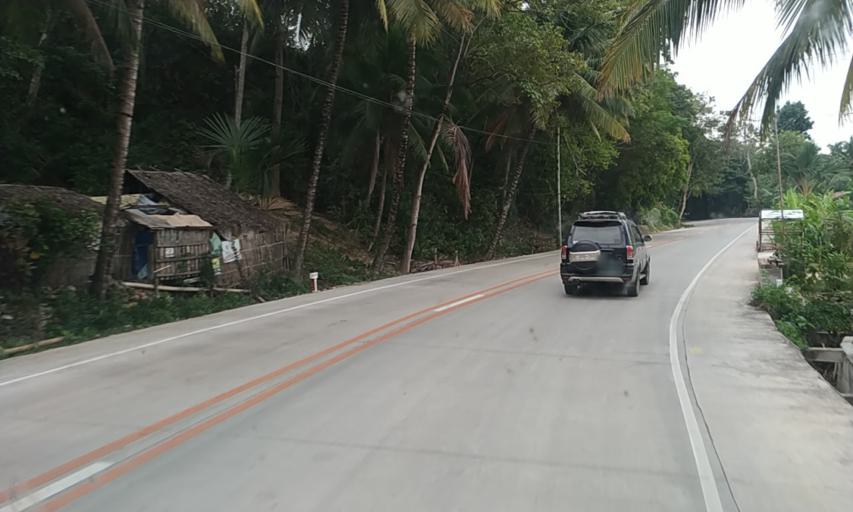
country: PH
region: Central Visayas
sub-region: Province of Negros Oriental
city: Basak
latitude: 10.2075
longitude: 123.3006
